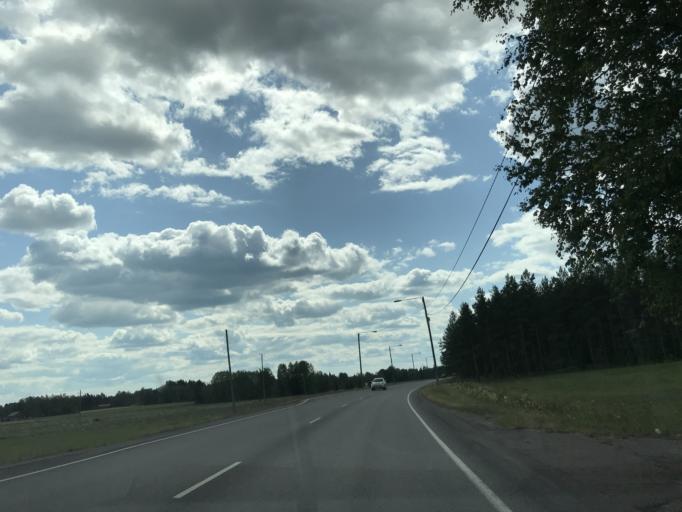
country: FI
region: Uusimaa
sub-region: Helsinki
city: Maentsaelae
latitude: 60.6536
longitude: 25.3422
